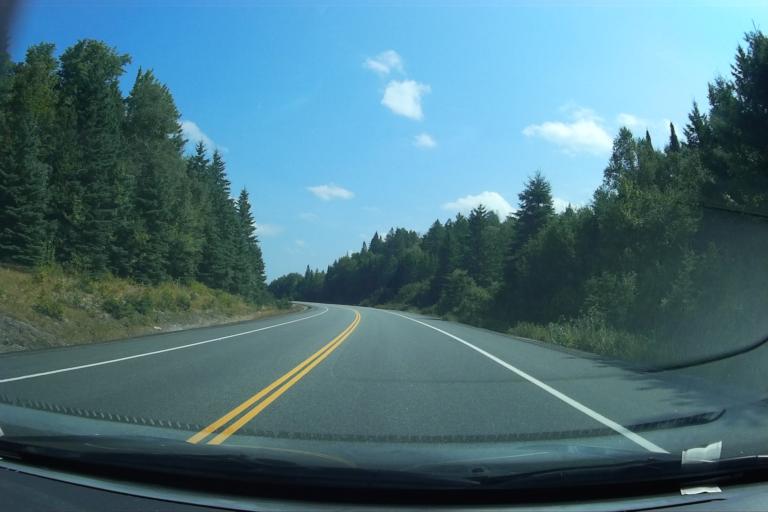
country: CA
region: Ontario
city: Huntsville
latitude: 45.5527
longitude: -78.6184
